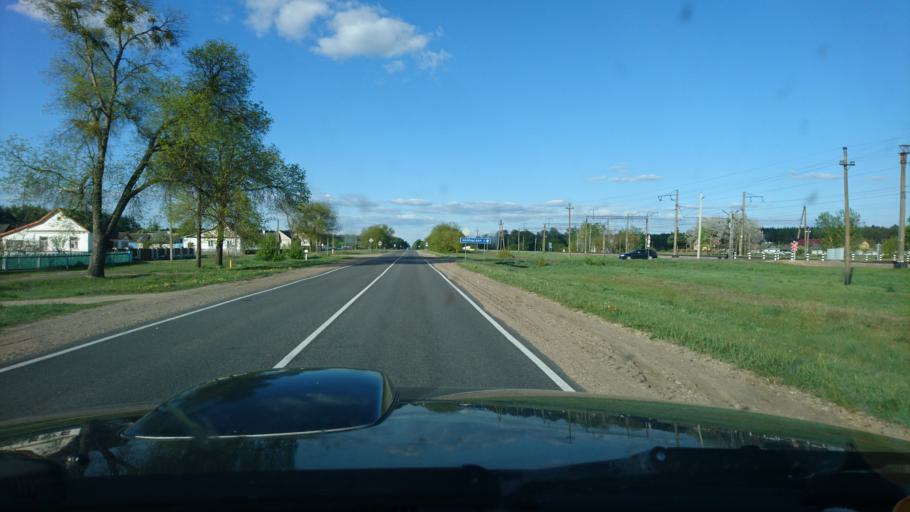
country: BY
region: Brest
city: Nyakhachava
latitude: 52.6482
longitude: 25.2140
